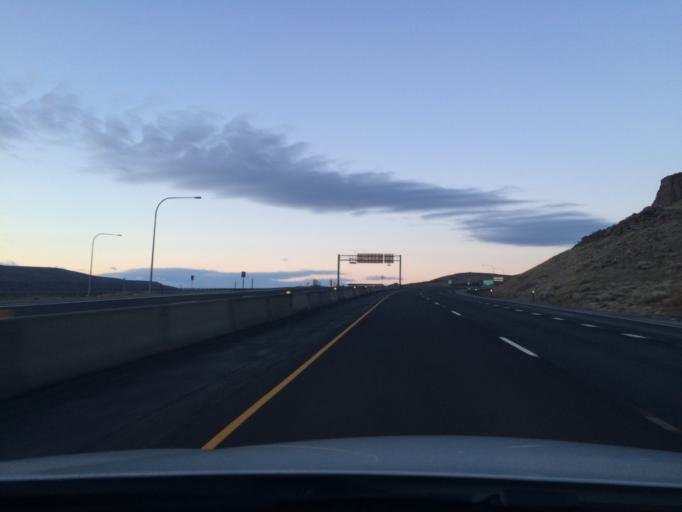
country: US
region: Washington
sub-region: Grant County
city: Mattawa
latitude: 46.9495
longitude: -119.9617
